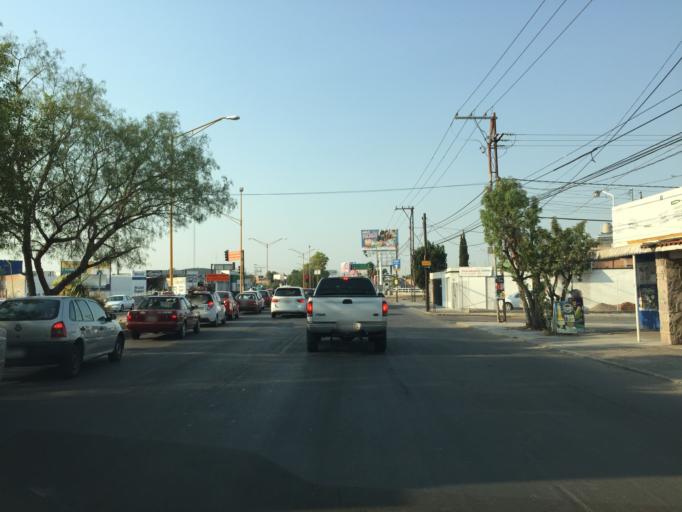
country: MX
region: Aguascalientes
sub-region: Aguascalientes
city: La Loma de los Negritos
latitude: 21.8691
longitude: -102.3184
